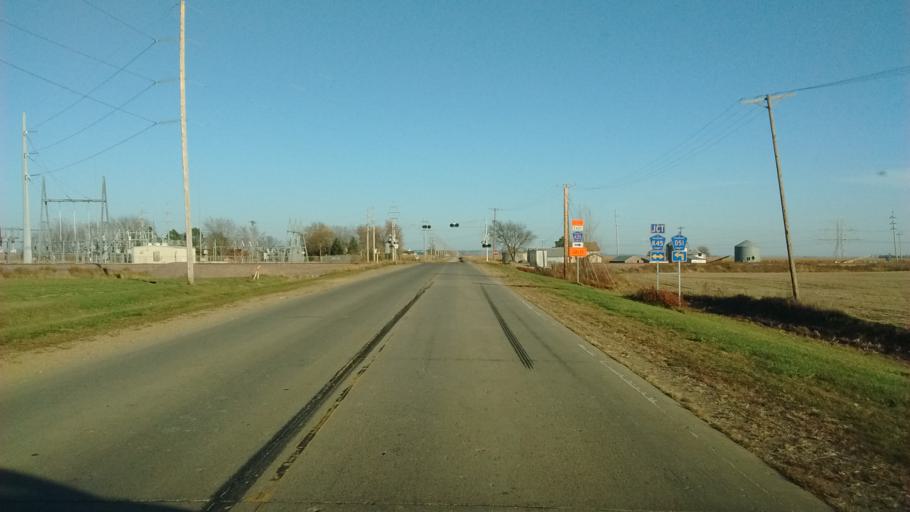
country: US
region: Iowa
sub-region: Woodbury County
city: Sergeant Bluff
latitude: 42.3302
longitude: -96.3037
